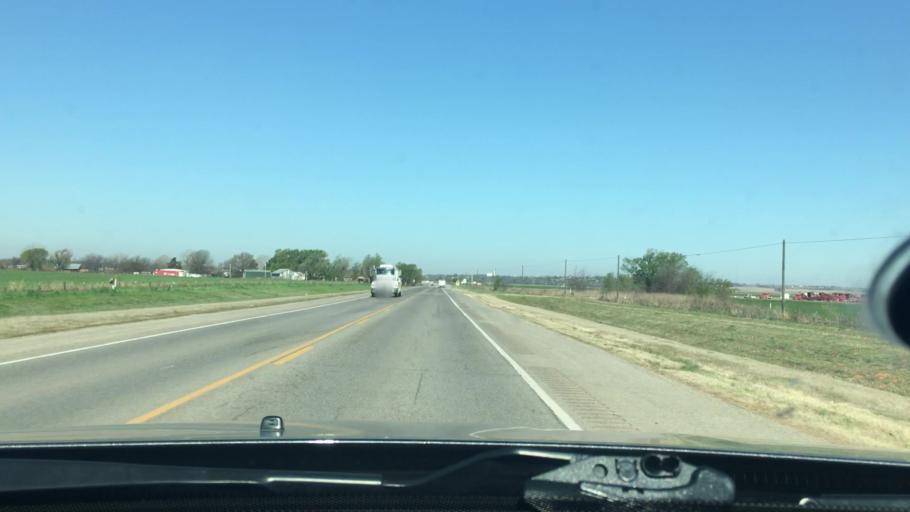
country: US
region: Oklahoma
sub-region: Garvin County
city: Lindsay
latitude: 34.8318
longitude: -97.5760
